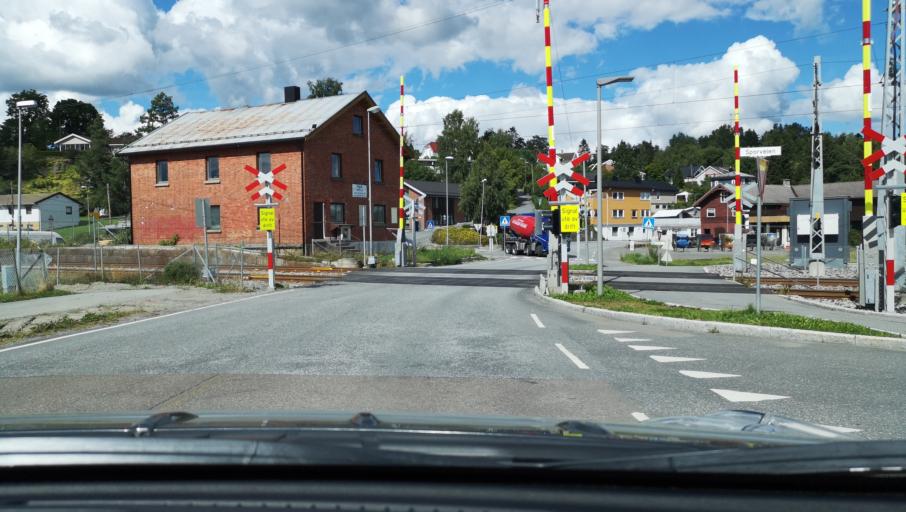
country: NO
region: Ostfold
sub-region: Hobol
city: Tomter
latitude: 59.6603
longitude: 11.0000
